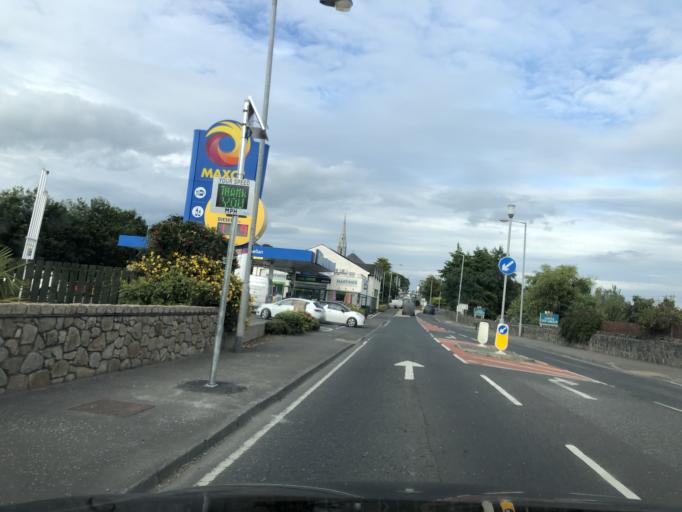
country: GB
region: Northern Ireland
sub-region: Down District
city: Castlewellan
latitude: 54.2551
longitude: -5.9506
